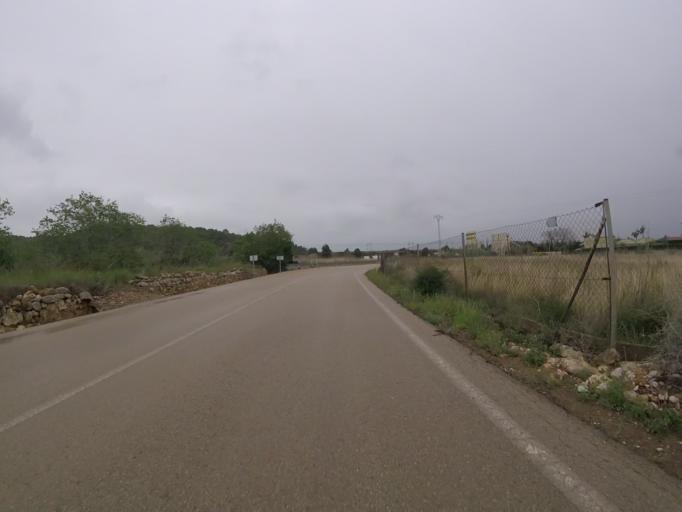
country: ES
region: Valencia
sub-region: Provincia de Castello
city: Alcoceber
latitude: 40.2536
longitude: 0.2463
